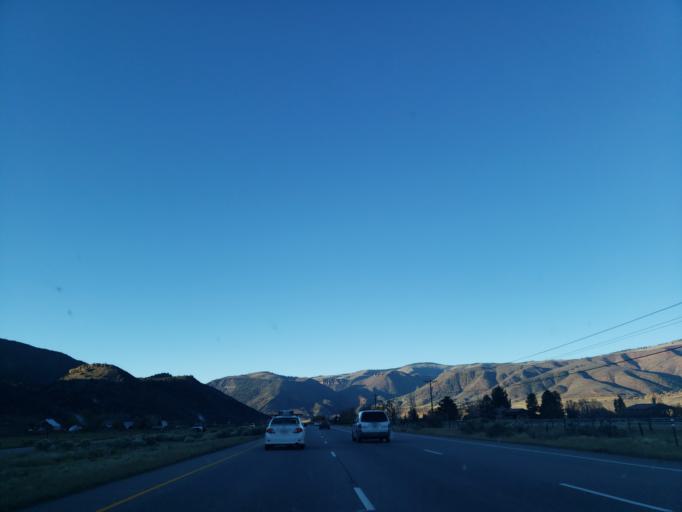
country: US
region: Colorado
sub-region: Pitkin County
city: Snowmass Village
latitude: 39.2526
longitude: -106.8847
